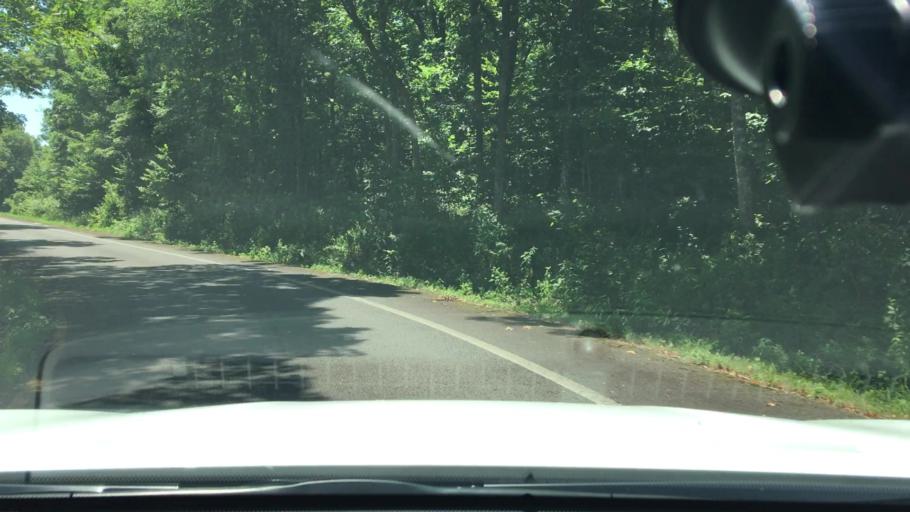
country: US
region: Arkansas
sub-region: Logan County
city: Paris
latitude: 35.1721
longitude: -93.6406
